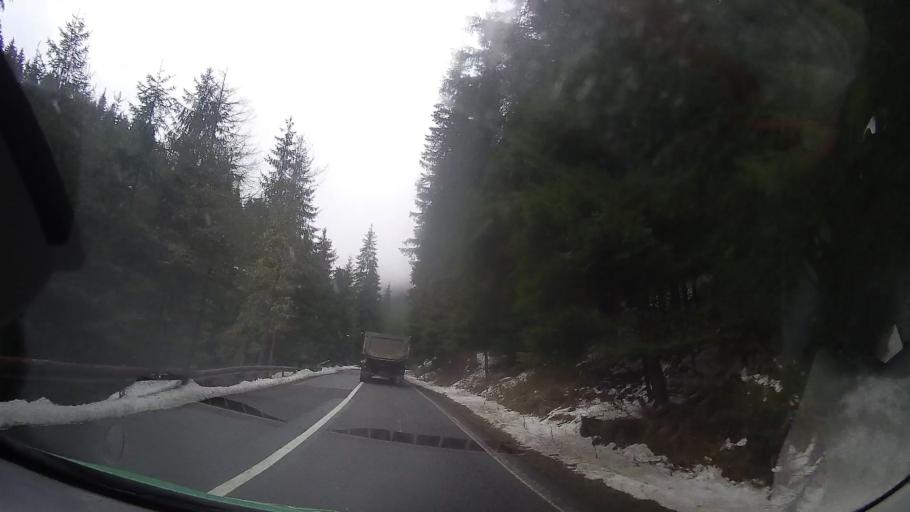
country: RO
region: Neamt
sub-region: Comuna Bicaz Chei
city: Bicaz Chei
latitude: 46.7811
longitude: 25.7503
